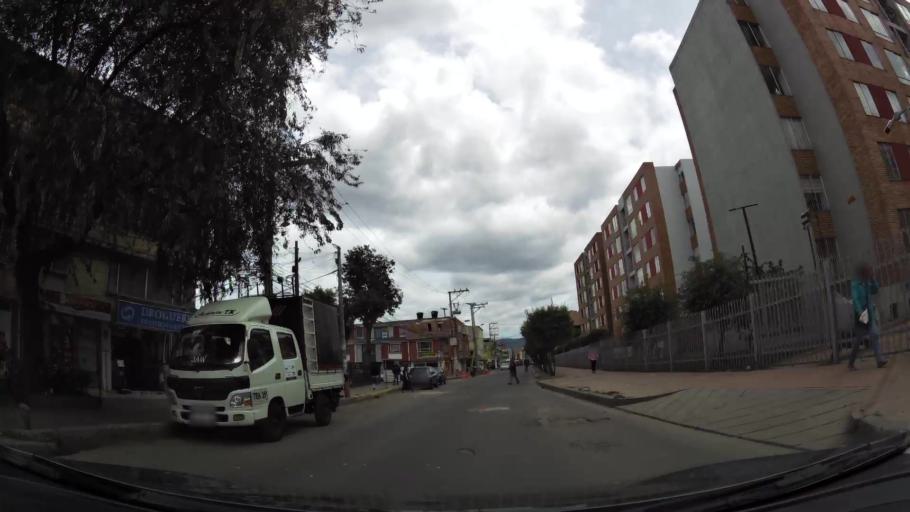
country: CO
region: Cundinamarca
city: Funza
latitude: 4.7154
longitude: -74.1283
